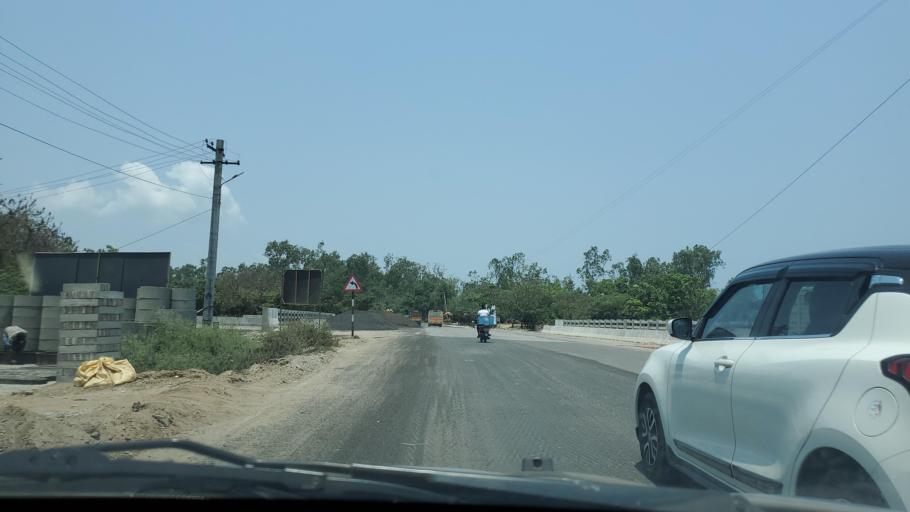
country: IN
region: Tamil Nadu
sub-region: Kancheepuram
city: Vengavasal
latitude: 12.8669
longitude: 80.1758
